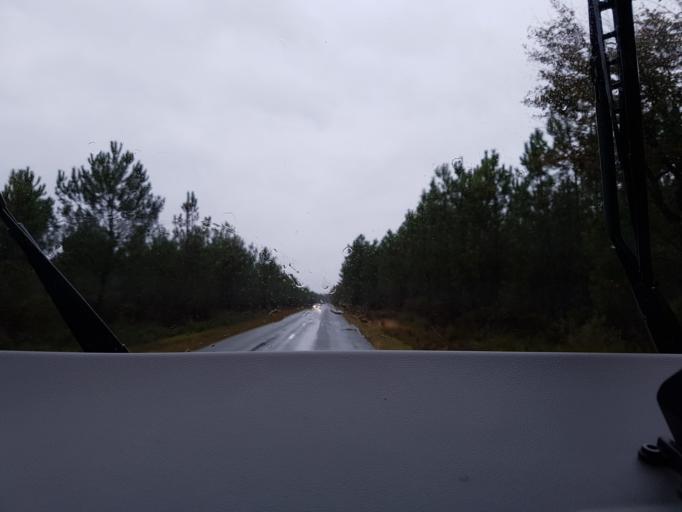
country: FR
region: Aquitaine
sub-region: Departement de la Gironde
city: Belin-Beliet
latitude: 44.5061
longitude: -0.7196
